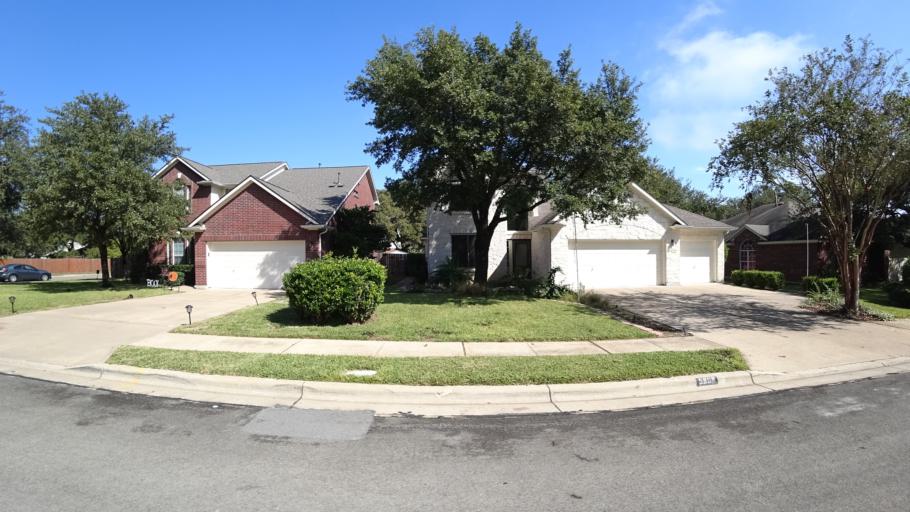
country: US
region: Texas
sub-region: Travis County
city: Shady Hollow
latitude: 30.2079
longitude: -97.8739
